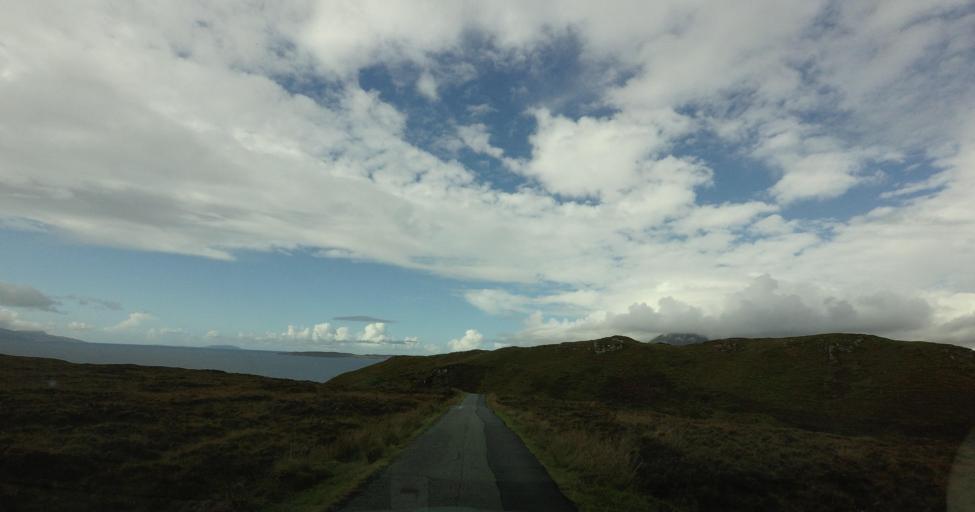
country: GB
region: Scotland
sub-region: Highland
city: Isle of Skye
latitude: 57.1458
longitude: -6.0931
